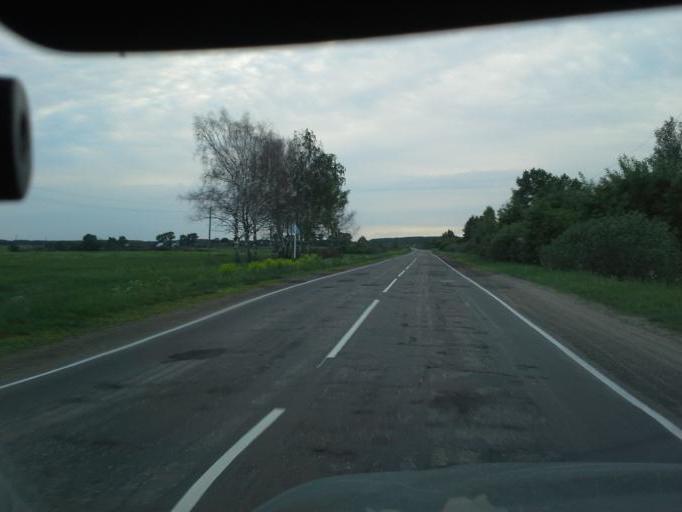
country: RU
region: Ivanovo
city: Petrovskiy
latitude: 56.6321
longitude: 40.2990
